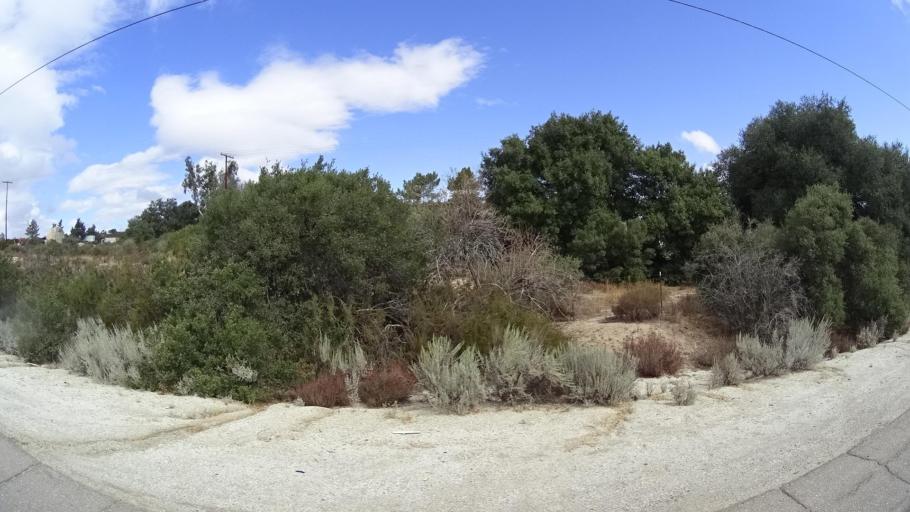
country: US
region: California
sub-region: San Diego County
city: Campo
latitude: 32.6691
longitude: -116.3061
